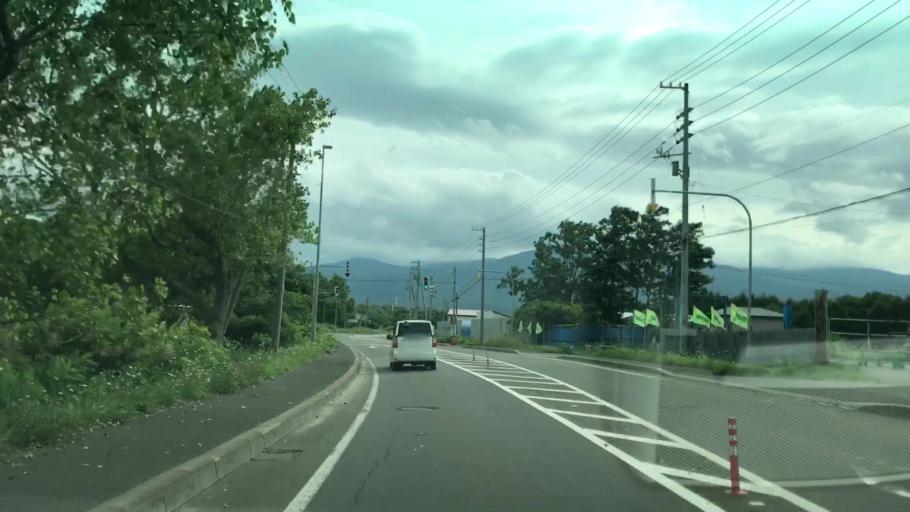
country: JP
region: Hokkaido
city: Iwanai
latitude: 43.0074
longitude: 140.5427
